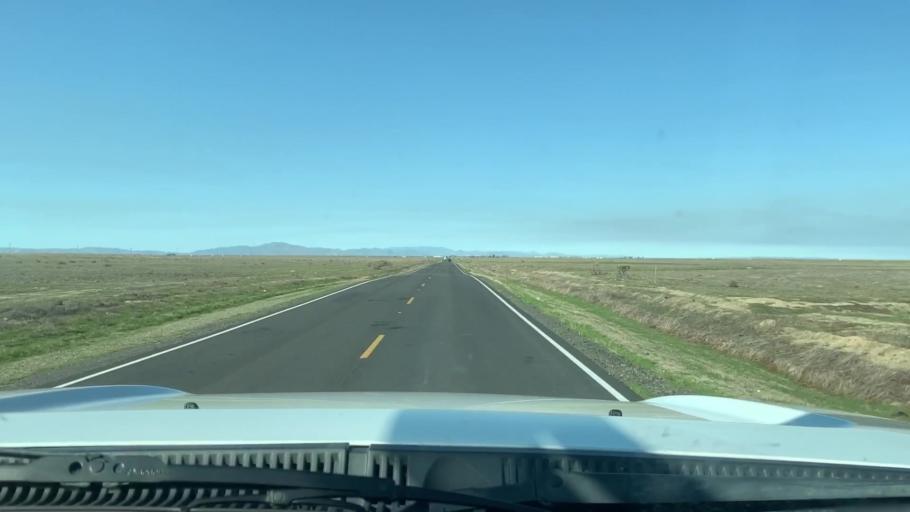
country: US
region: California
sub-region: Kern County
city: Lost Hills
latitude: 35.5735
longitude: -119.8168
